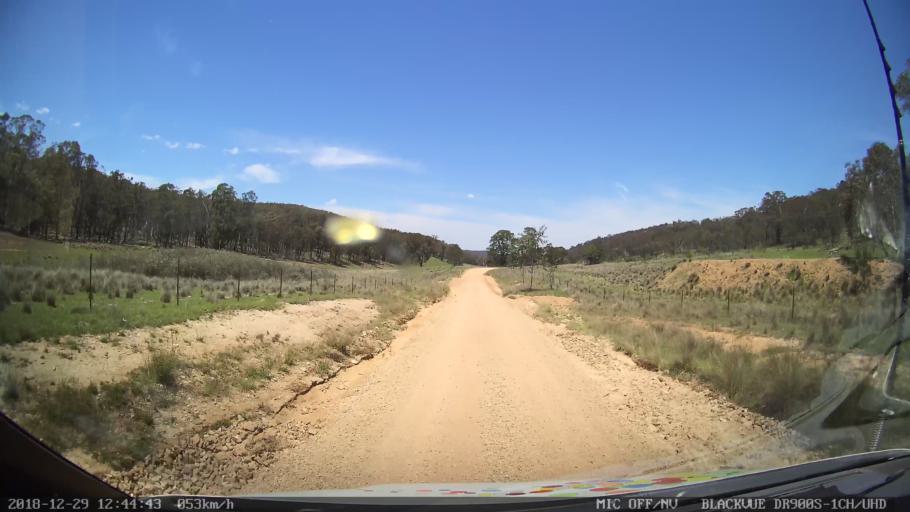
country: AU
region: Australian Capital Territory
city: Macarthur
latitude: -35.6296
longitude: 149.2158
